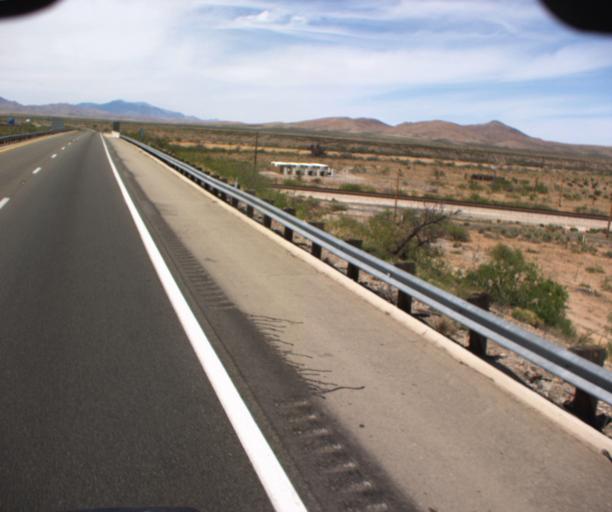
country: US
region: Arizona
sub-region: Cochise County
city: Willcox
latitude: 32.3518
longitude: -109.6075
